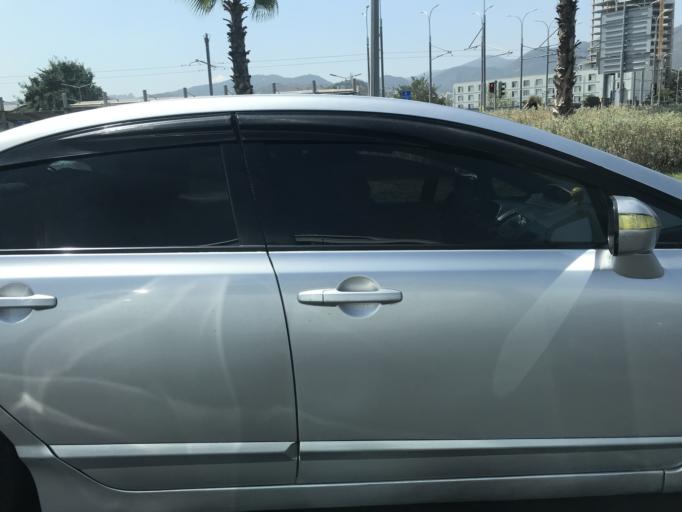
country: TR
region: Izmir
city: Karsiyaka
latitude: 38.4036
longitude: 27.0715
